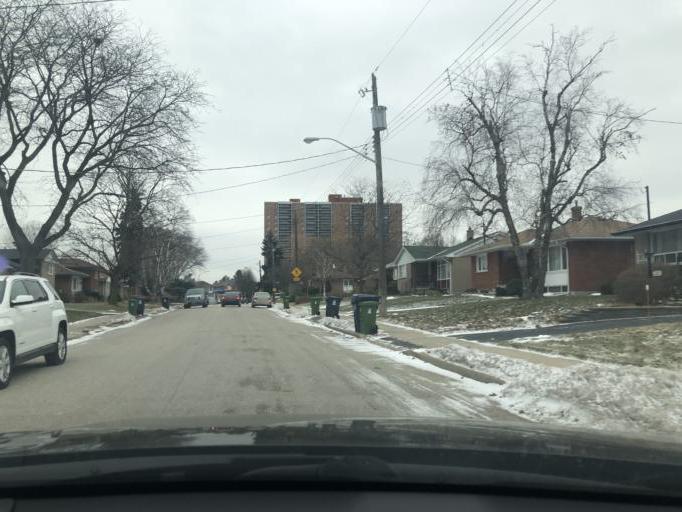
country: CA
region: Ontario
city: Scarborough
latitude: 43.7763
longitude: -79.3143
